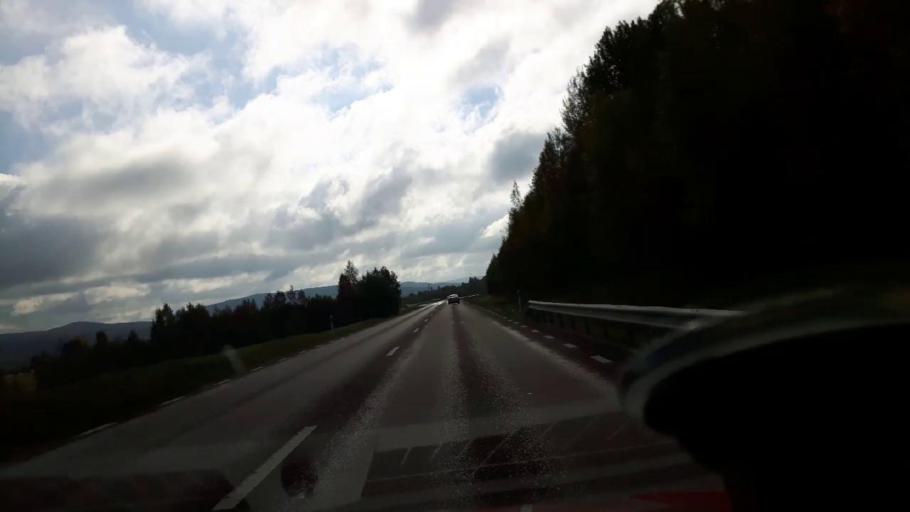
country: SE
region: Gaevleborg
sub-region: Ljusdals Kommun
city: Jaervsoe
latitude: 61.7310
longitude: 16.1653
